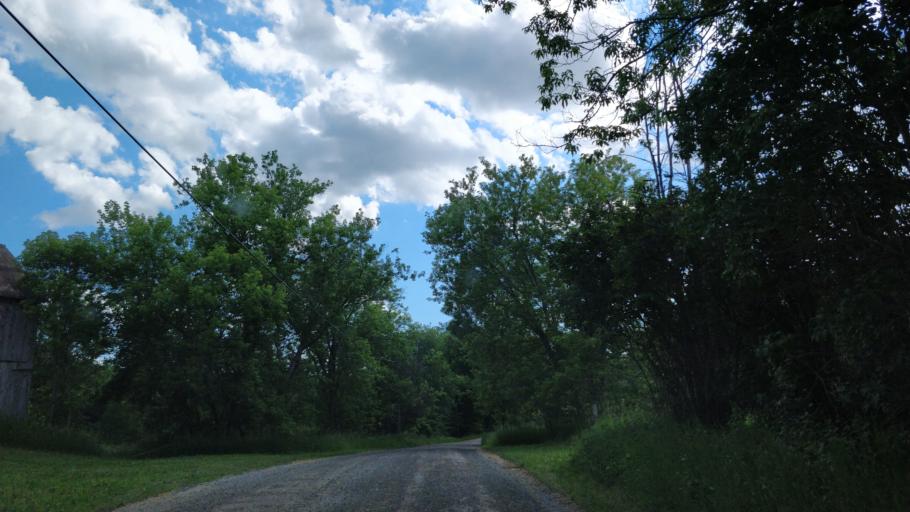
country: CA
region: Ontario
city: Perth
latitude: 44.6646
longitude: -76.5383
